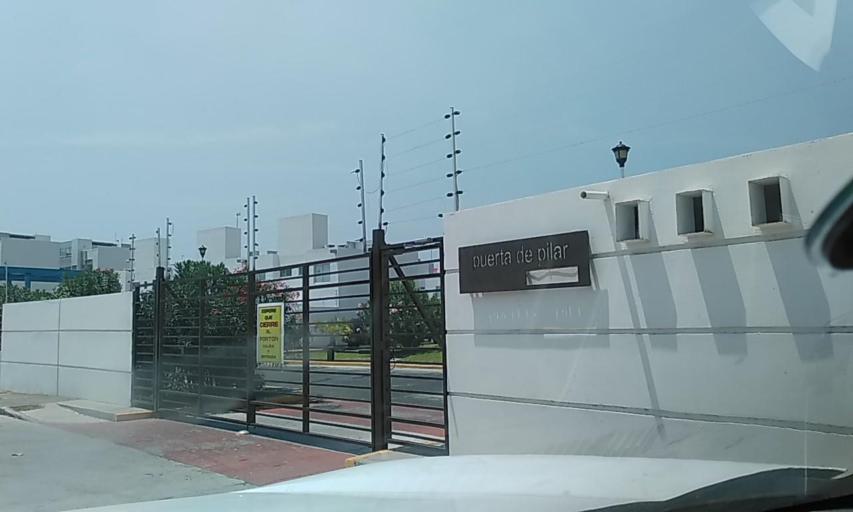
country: MX
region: Veracruz
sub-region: Veracruz
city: Hacienda Sotavento
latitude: 19.1242
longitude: -96.1706
